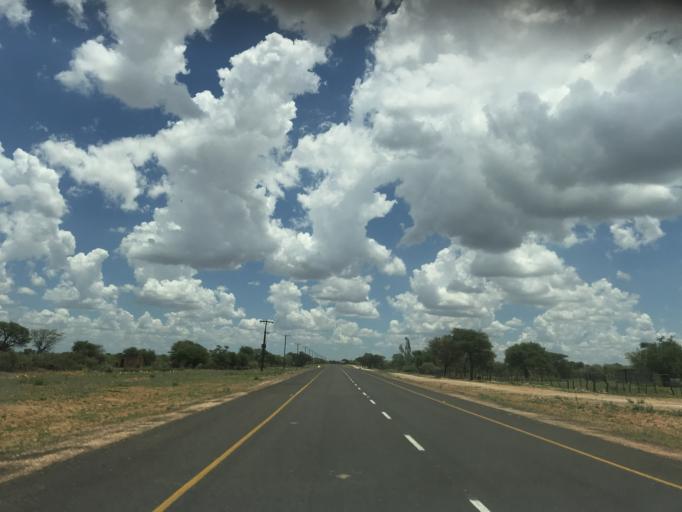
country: BW
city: Mabuli
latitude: -25.8037
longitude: 24.8271
